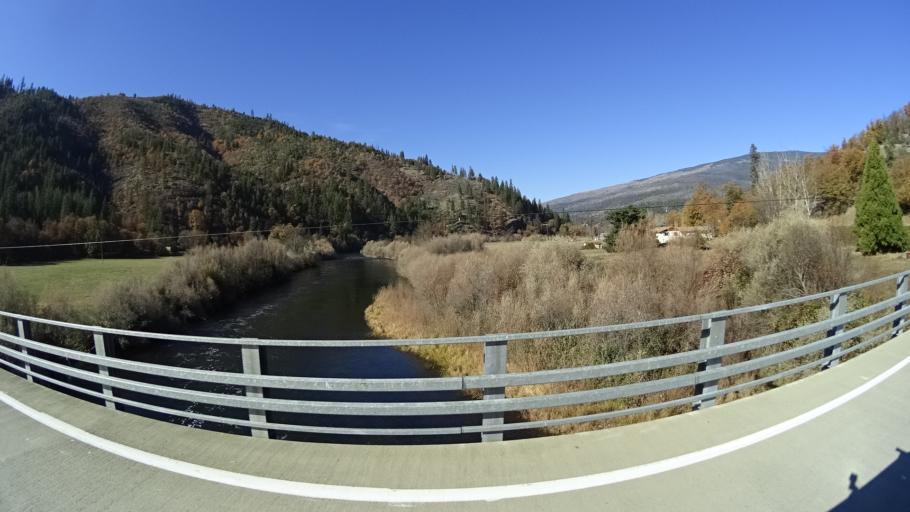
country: US
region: California
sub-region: Siskiyou County
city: Yreka
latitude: 41.8374
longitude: -122.8646
